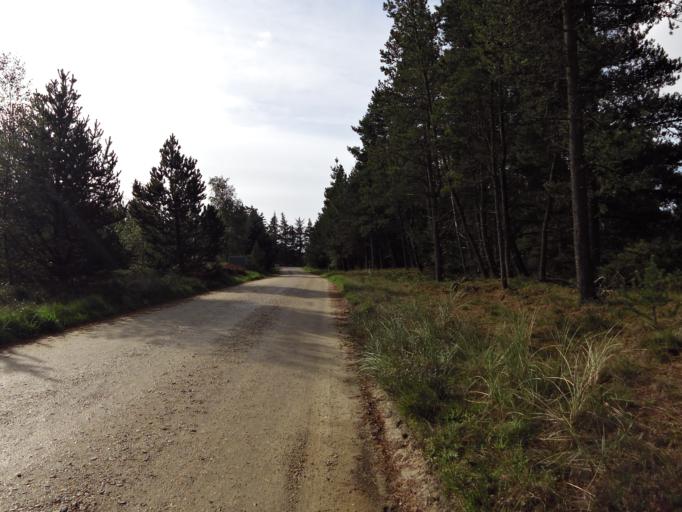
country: DK
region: South Denmark
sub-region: Varde Kommune
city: Oksbol
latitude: 55.5514
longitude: 8.2110
